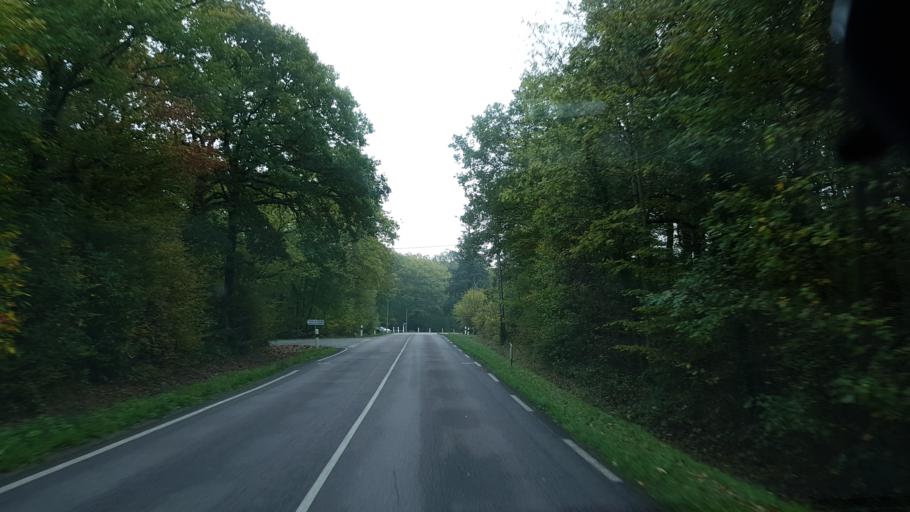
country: FR
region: Ile-de-France
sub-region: Departement de l'Essonne
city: Dourdan
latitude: 48.5430
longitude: 1.9935
